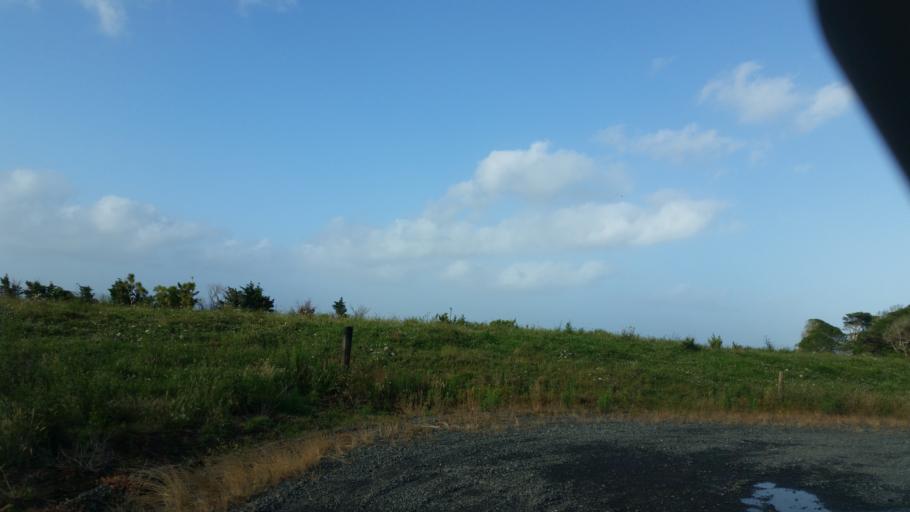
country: NZ
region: Northland
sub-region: Far North District
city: Kaitaia
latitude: -35.1002
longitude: 173.2293
